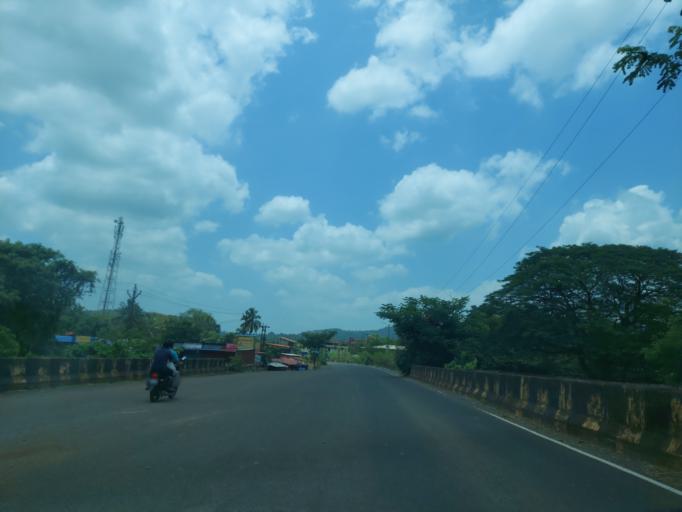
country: IN
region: Maharashtra
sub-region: Sindhudurg
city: Savantvadi
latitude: 15.8187
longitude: 73.8627
